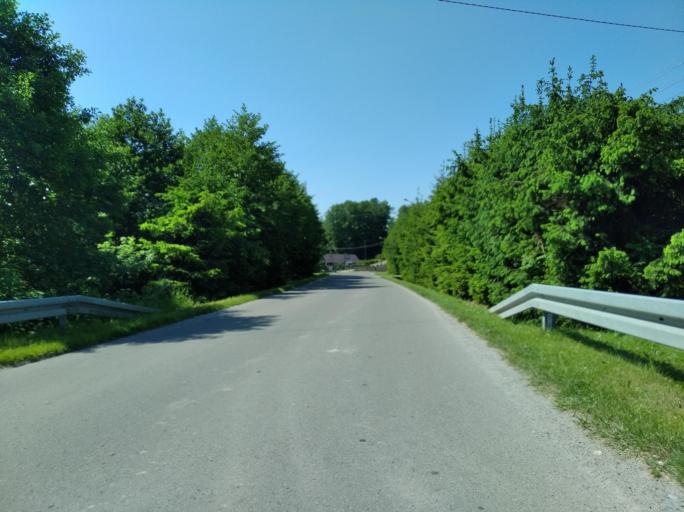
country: PL
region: Subcarpathian Voivodeship
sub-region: Powiat ropczycko-sedziszowski
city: Zagorzyce
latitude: 50.0084
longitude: 21.6585
